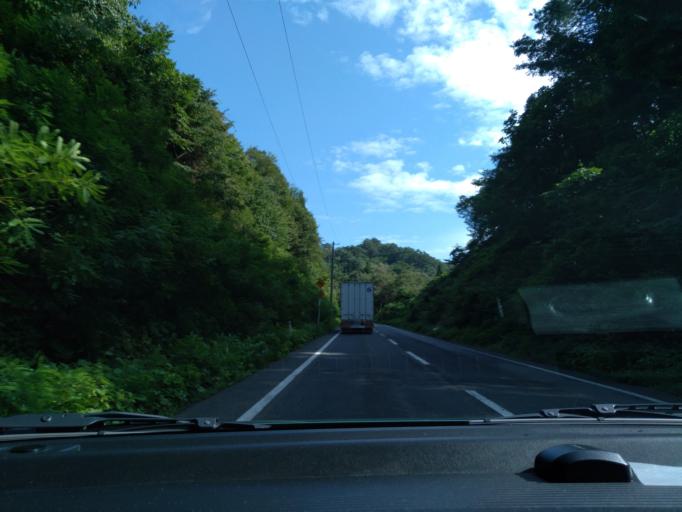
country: JP
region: Iwate
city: Shizukuishi
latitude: 39.6387
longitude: 141.0166
